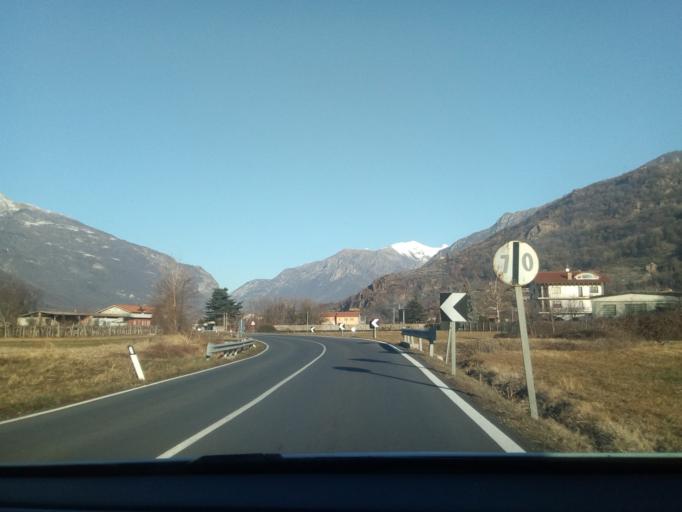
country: IT
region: Piedmont
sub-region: Provincia di Torino
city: Nomaglio
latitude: 45.5288
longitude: 7.8487
